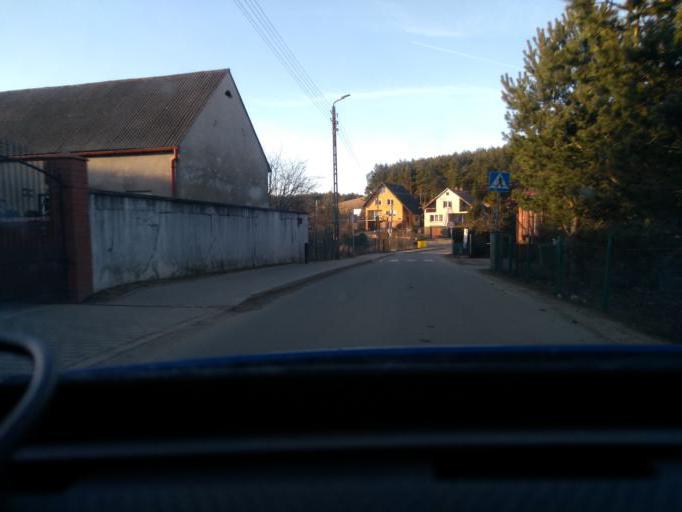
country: PL
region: Pomeranian Voivodeship
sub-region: Powiat kartuski
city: Przodkowo
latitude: 54.3778
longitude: 18.2638
